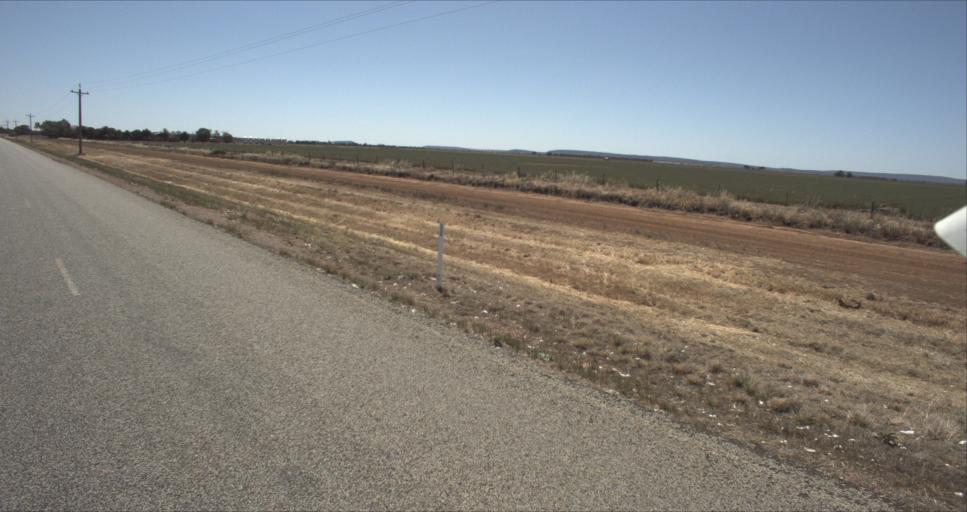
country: AU
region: New South Wales
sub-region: Leeton
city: Leeton
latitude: -34.4558
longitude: 146.2951
